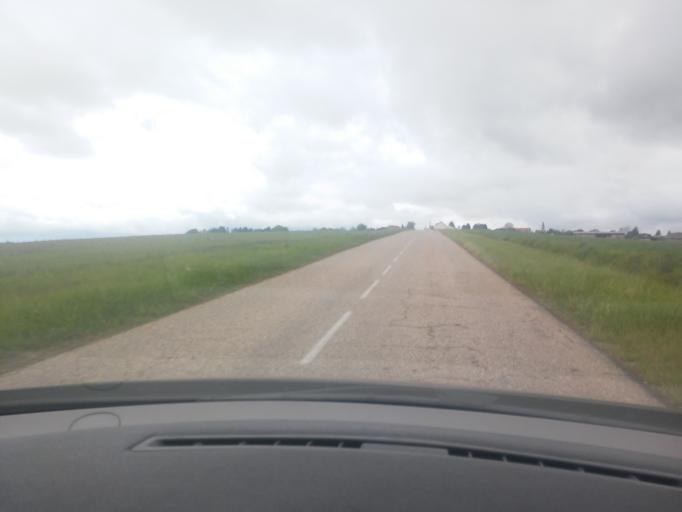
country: FR
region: Lorraine
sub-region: Departement de la Moselle
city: Retonfey
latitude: 49.0763
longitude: 6.3351
